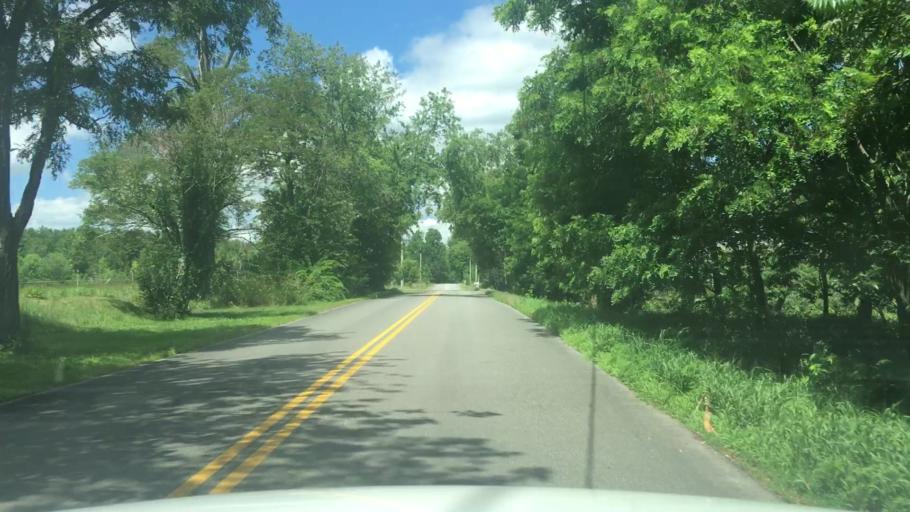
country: US
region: Maine
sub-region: Waldo County
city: Belfast
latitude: 44.4115
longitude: -69.0376
